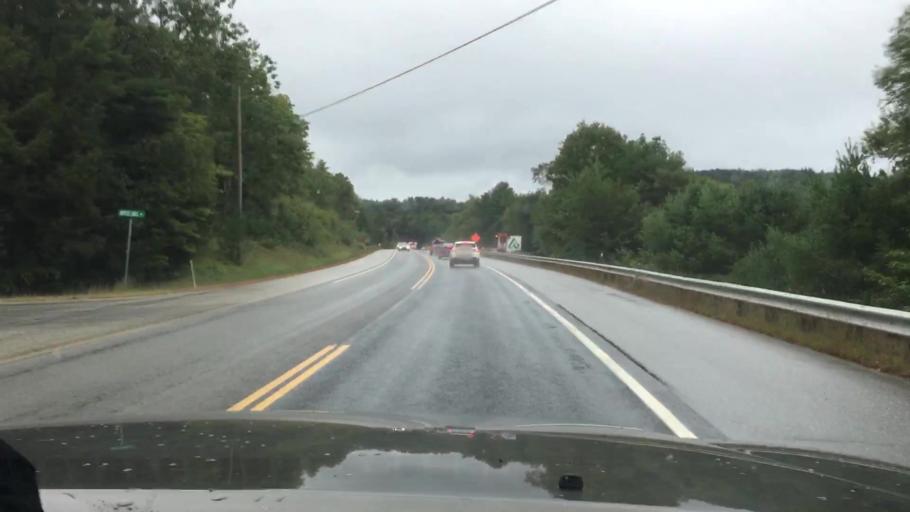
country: US
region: New Hampshire
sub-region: Cheshire County
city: Marlborough
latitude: 42.9961
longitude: -72.1902
